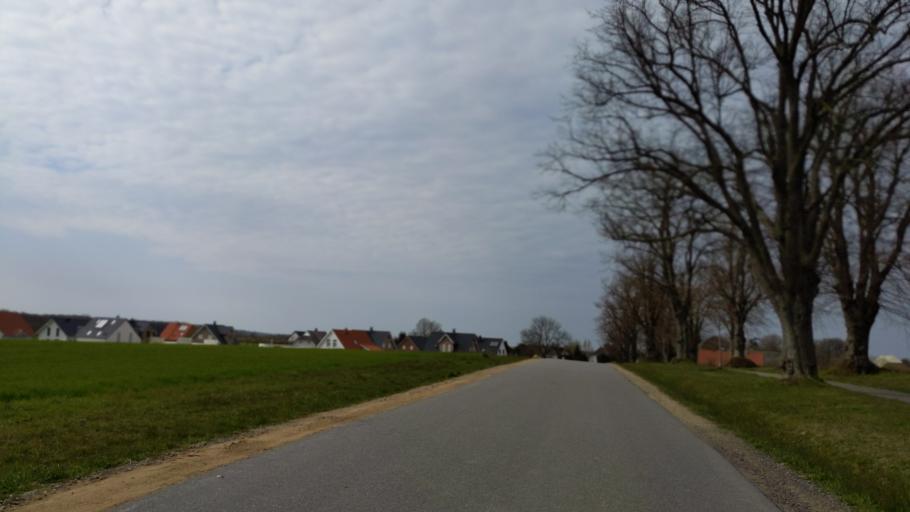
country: DE
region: Mecklenburg-Vorpommern
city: Dassow
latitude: 53.9628
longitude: 10.9689
